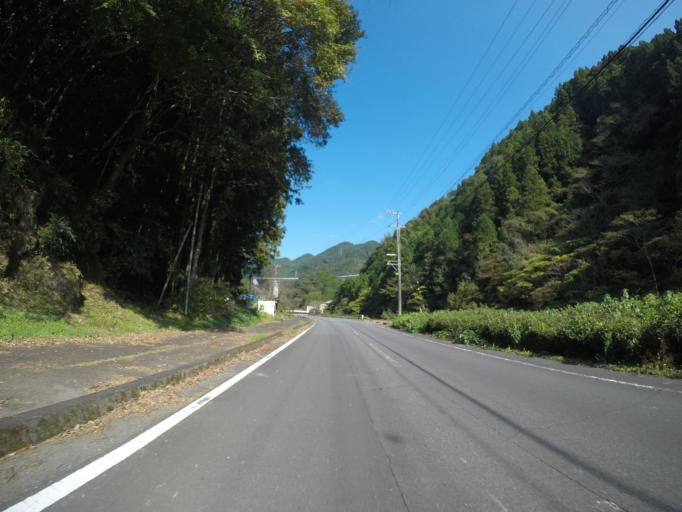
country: JP
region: Shizuoka
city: Shizuoka-shi
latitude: 35.1152
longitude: 138.4521
